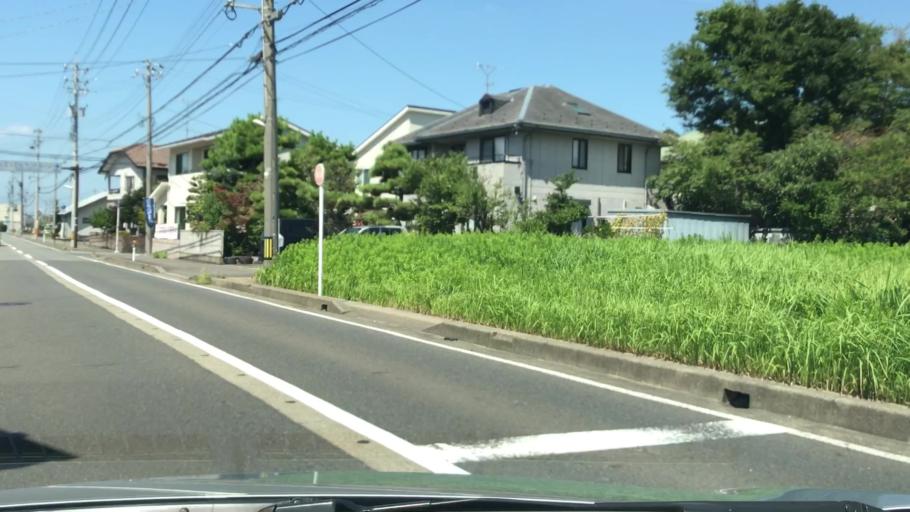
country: JP
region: Fukui
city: Maruoka
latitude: 36.1286
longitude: 136.2179
